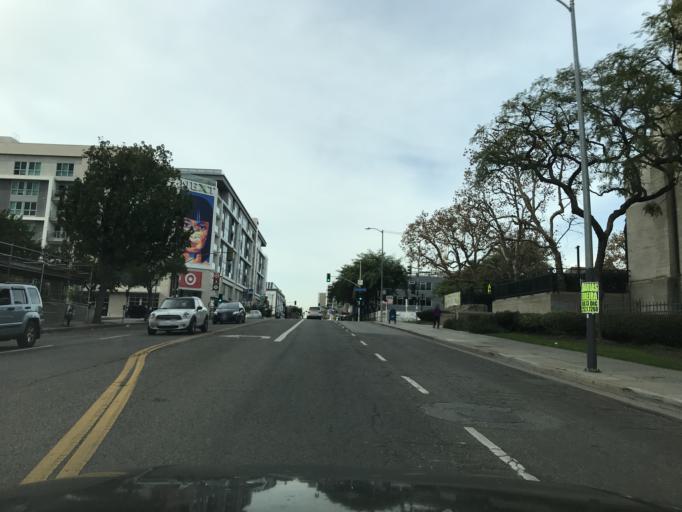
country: US
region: California
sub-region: Los Angeles County
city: Silver Lake
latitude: 34.0637
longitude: -118.2849
